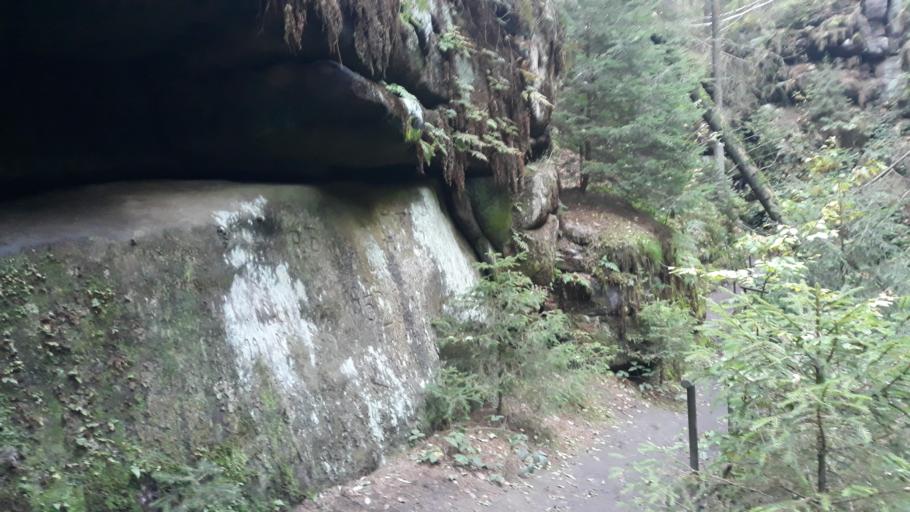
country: DE
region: Saxony
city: Stadt Wehlen
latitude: 50.9668
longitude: 14.0285
